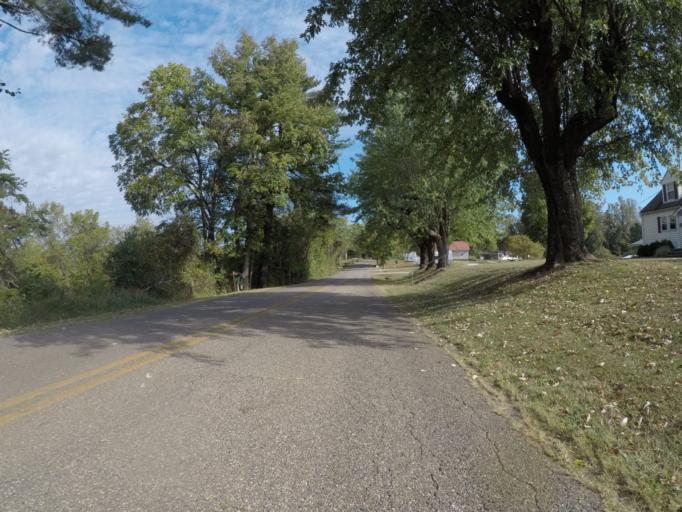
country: US
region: West Virginia
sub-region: Cabell County
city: Lesage
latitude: 38.5551
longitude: -82.4261
